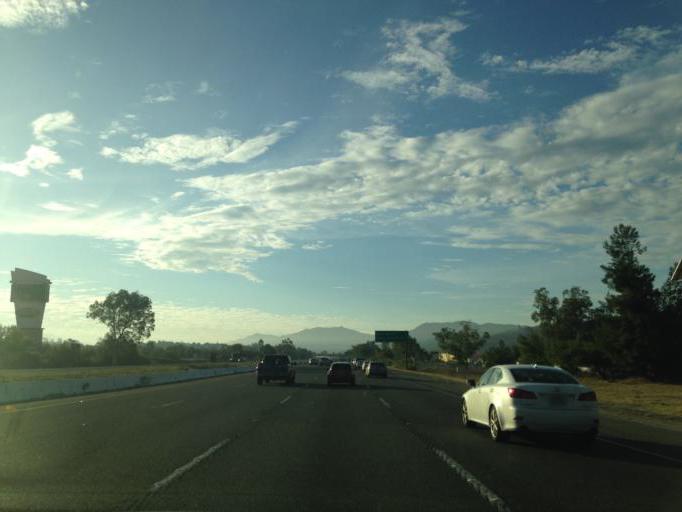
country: US
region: California
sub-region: Riverside County
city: Temecula
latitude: 33.5116
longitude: -117.1565
